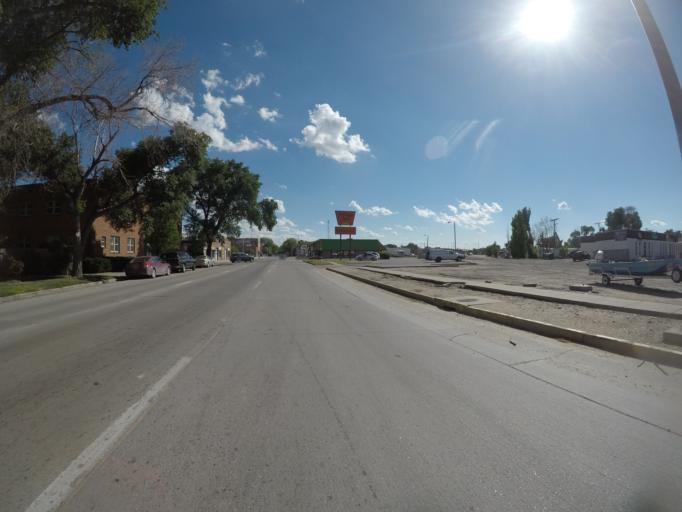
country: US
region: Colorado
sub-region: Logan County
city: Sterling
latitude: 40.6267
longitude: -103.2083
